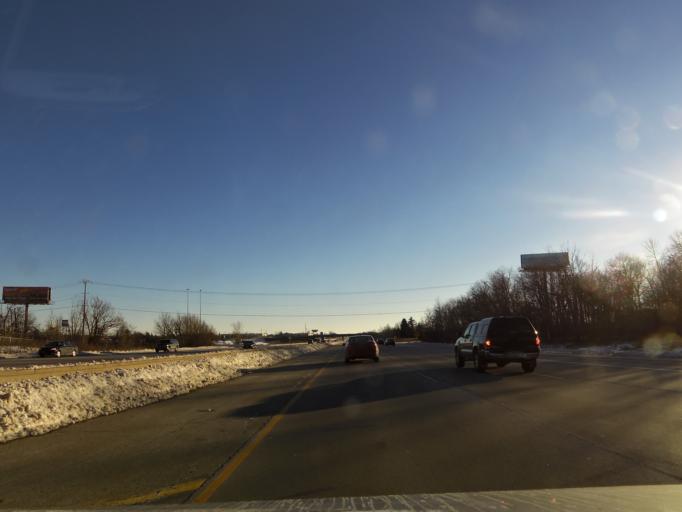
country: US
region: Wisconsin
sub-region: Racine County
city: Caledonia
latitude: 42.8772
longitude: -87.9372
